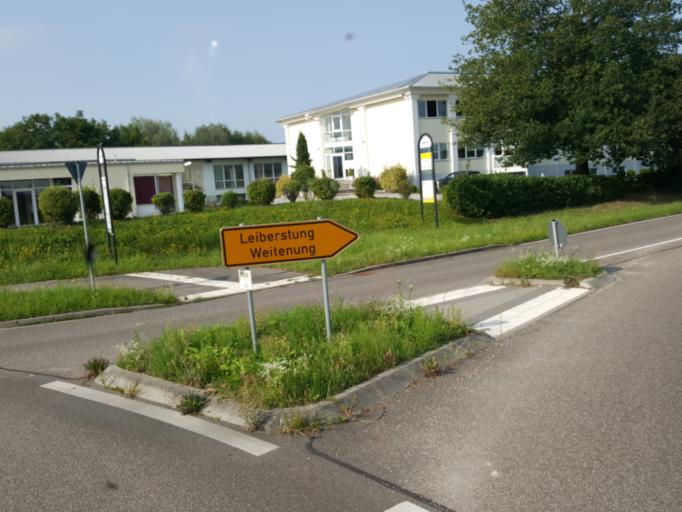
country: DE
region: Baden-Wuerttemberg
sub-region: Karlsruhe Region
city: Ottenhofen
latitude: 48.7353
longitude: 8.1447
